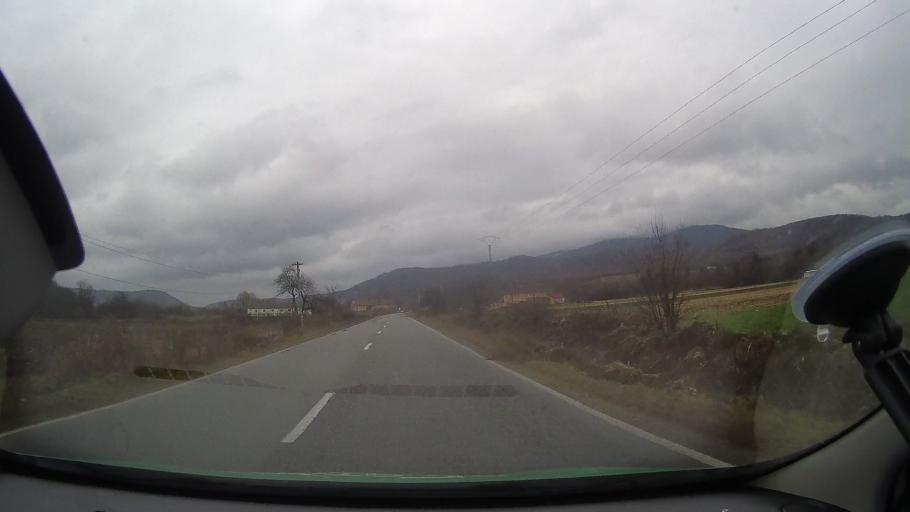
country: RO
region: Arad
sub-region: Comuna Buteni
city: Buteni
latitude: 46.3133
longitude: 22.1409
